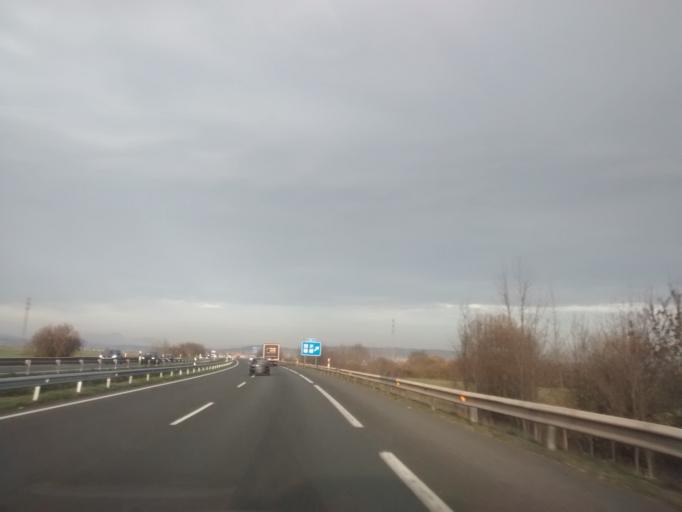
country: ES
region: Basque Country
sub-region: Provincia de Alava
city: Gasteiz / Vitoria
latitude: 42.8703
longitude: -2.7210
